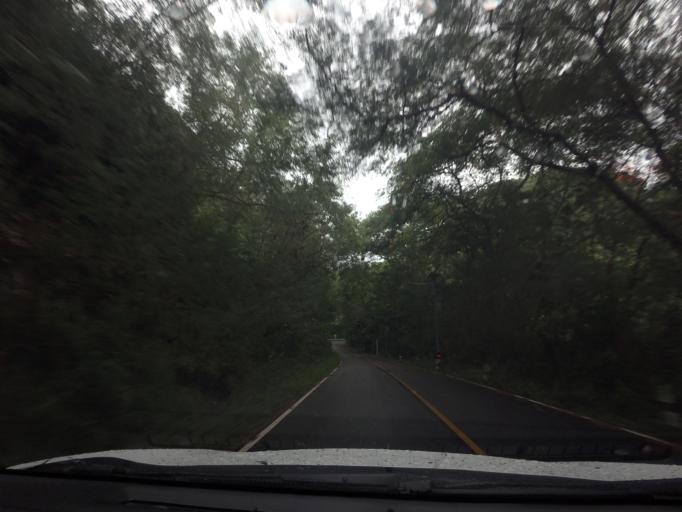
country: TH
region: Rayong
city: Ban Chang
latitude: 12.7636
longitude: 100.9527
